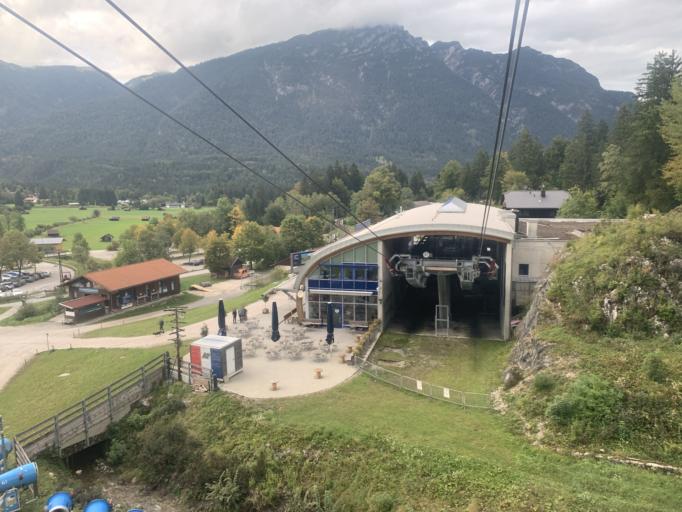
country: DE
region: Bavaria
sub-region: Upper Bavaria
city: Garmisch-Partenkirchen
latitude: 47.4710
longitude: 11.0639
